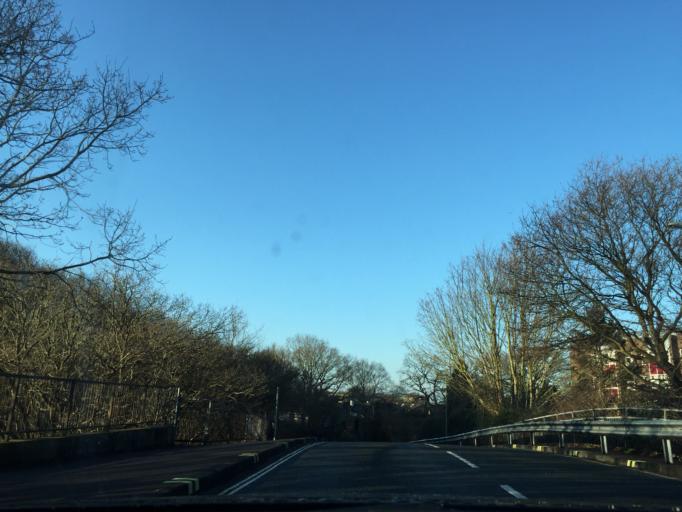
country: GB
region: England
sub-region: Hampshire
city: Fareham
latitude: 50.8197
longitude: -1.1663
